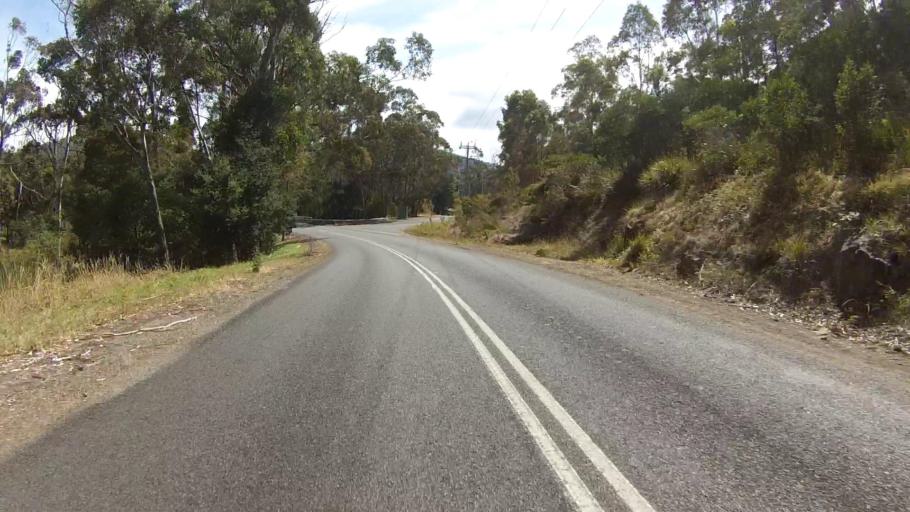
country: AU
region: Tasmania
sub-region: Huon Valley
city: Cygnet
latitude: -43.2422
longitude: 147.1511
